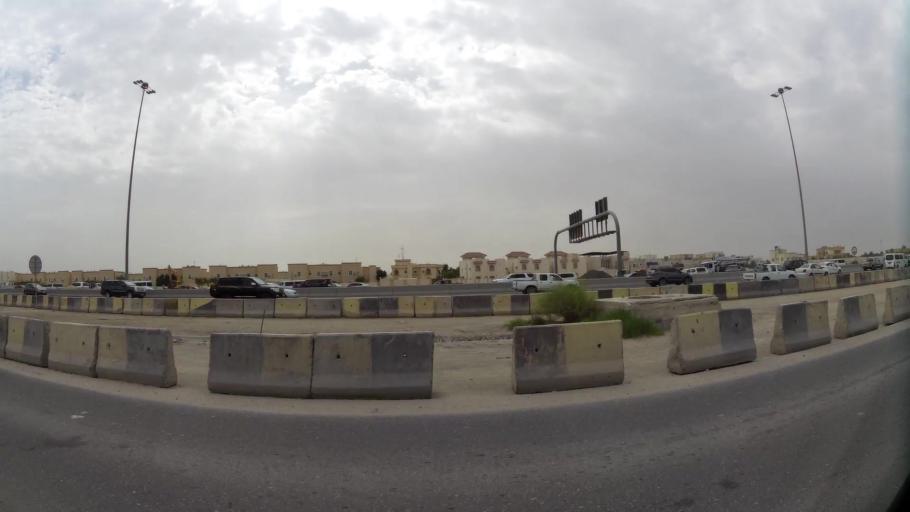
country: QA
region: Baladiyat ar Rayyan
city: Ar Rayyan
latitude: 25.3503
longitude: 51.4556
